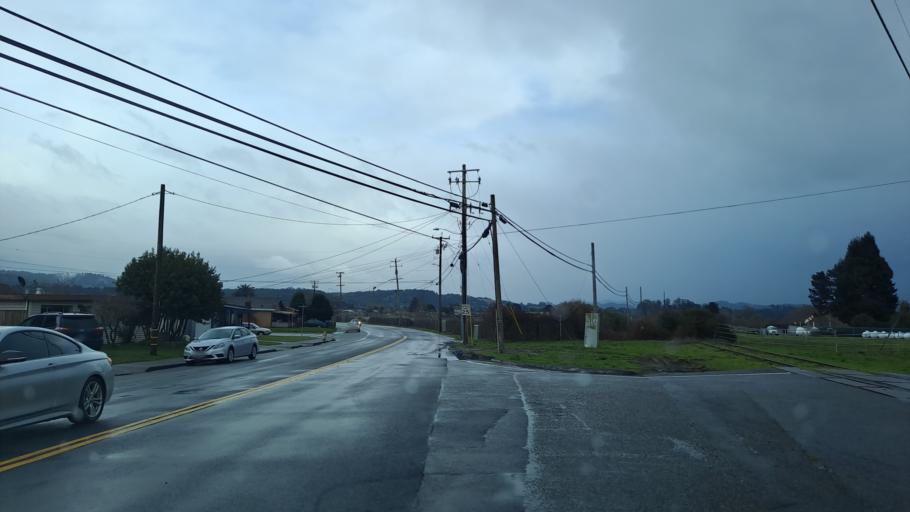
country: US
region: California
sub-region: Humboldt County
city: Fortuna
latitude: 40.5898
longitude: -124.1545
